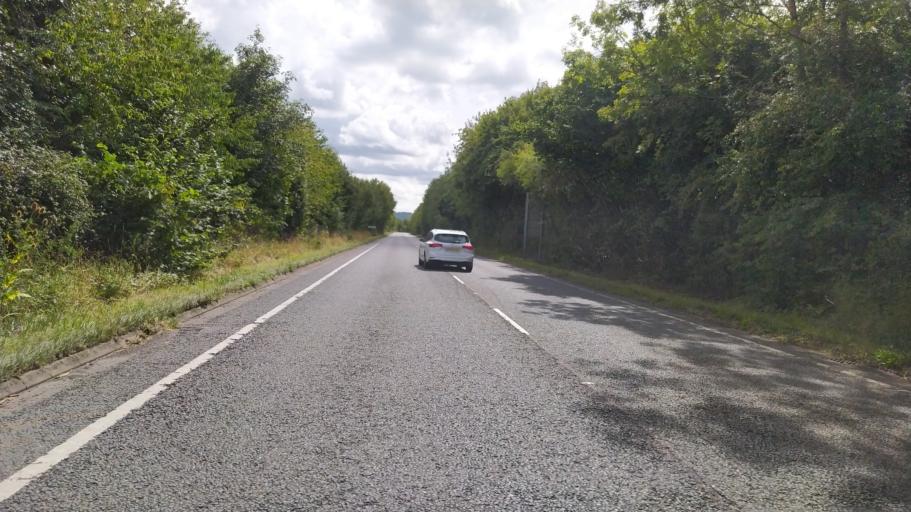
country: GB
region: England
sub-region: Wiltshire
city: Hindon
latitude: 51.0743
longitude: -2.1681
